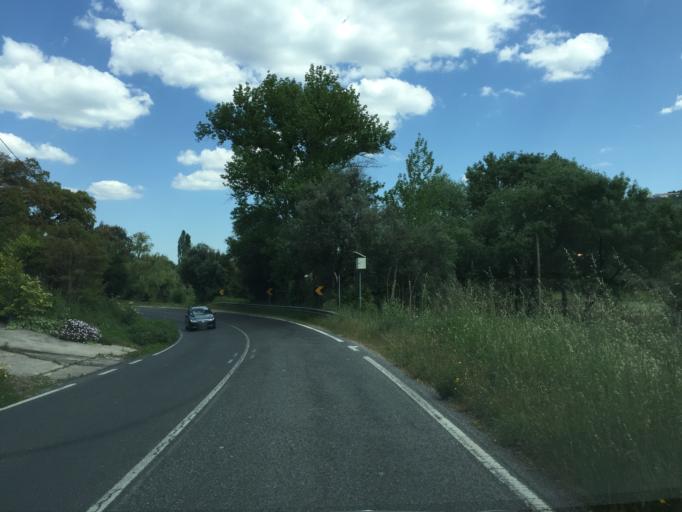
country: PT
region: Santarem
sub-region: Ourem
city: Ourem
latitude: 39.6533
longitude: -8.6028
